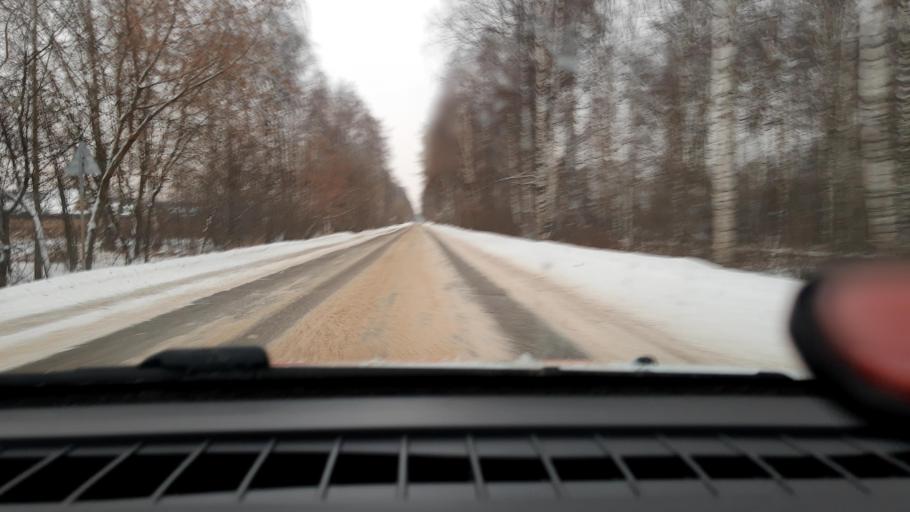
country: RU
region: Nizjnij Novgorod
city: Pamyat' Parizhskoy Kommuny
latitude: 56.2694
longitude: 44.4220
